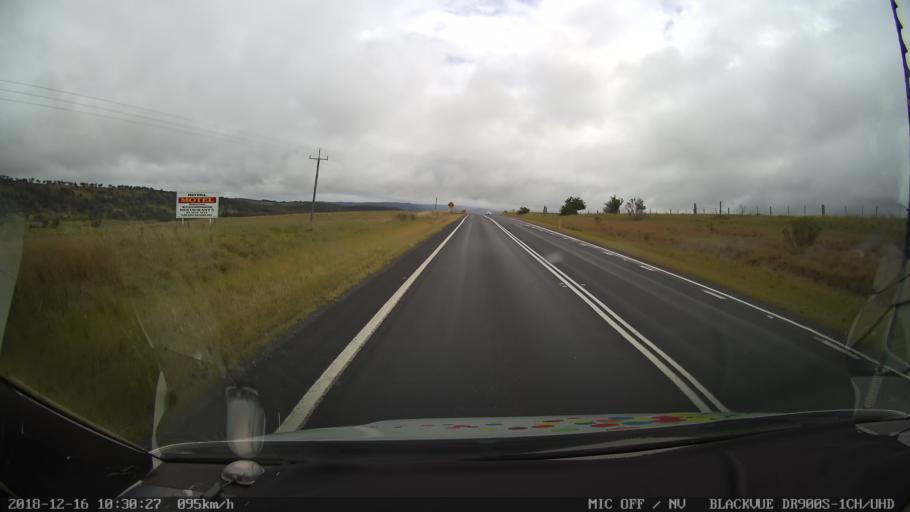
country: AU
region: New South Wales
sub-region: Tenterfield Municipality
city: Carrolls Creek
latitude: -29.0930
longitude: 152.0026
